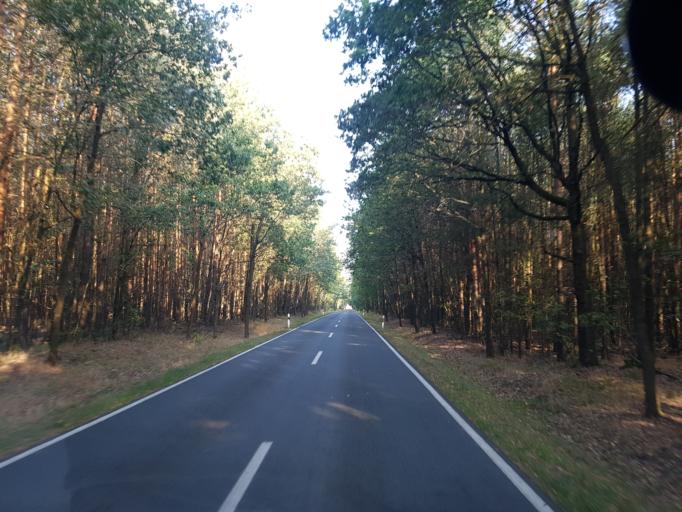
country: DE
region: Brandenburg
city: Sonnewalde
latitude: 51.6799
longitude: 13.6928
